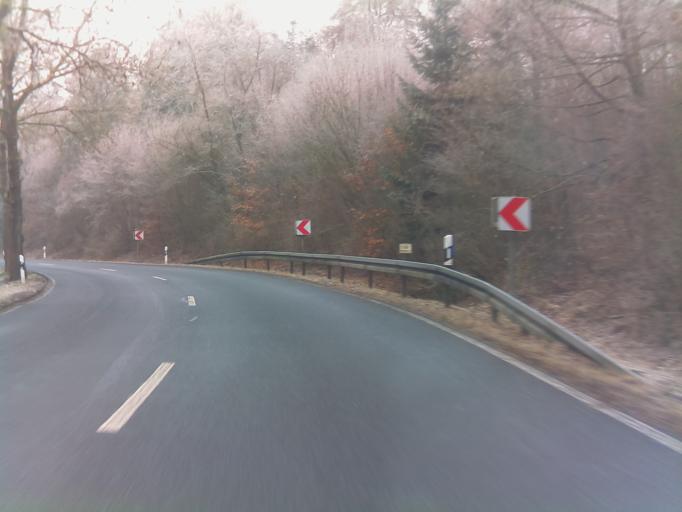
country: DE
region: Thuringia
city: Kuhndorf
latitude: 50.5975
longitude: 10.4651
